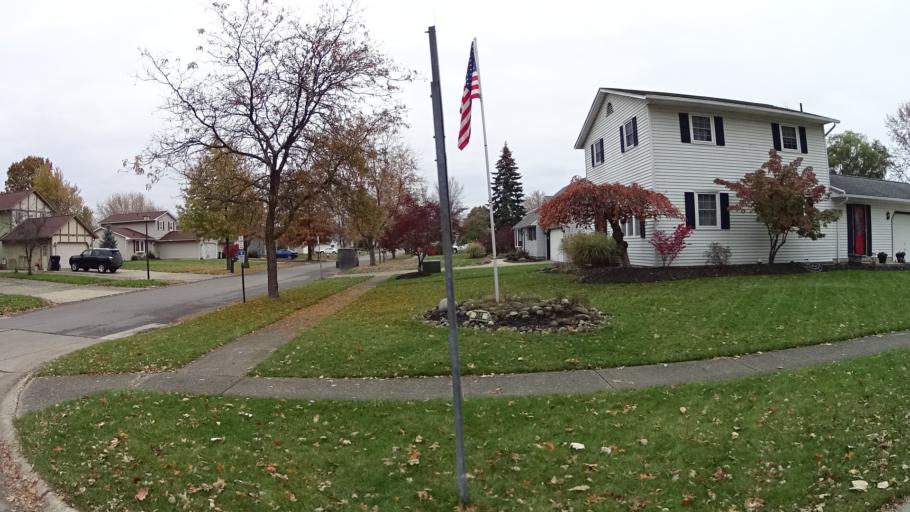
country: US
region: Ohio
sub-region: Lorain County
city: Sheffield
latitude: 41.4164
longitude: -82.0830
